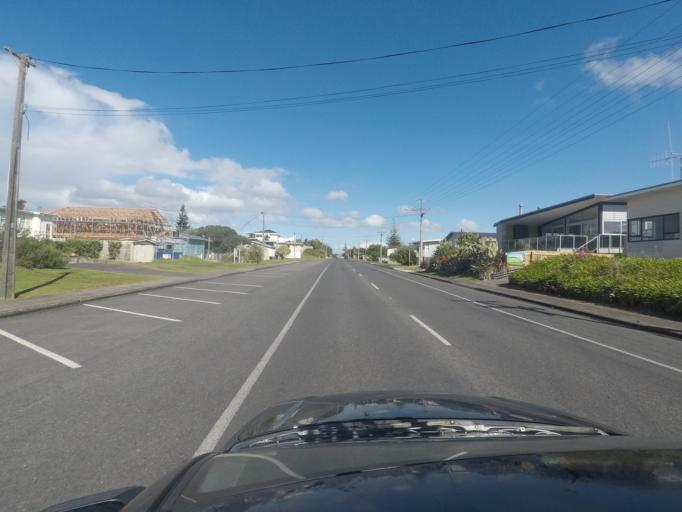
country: NZ
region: Bay of Plenty
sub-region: Western Bay of Plenty District
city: Waihi Beach
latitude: -37.4135
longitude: 175.9465
